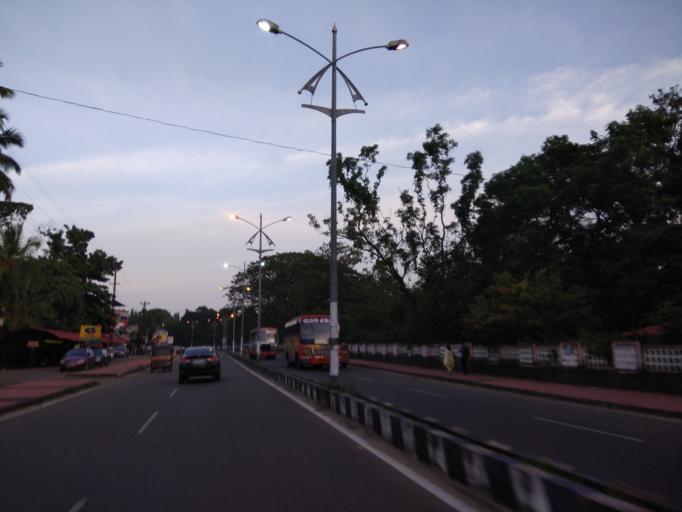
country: IN
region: Kerala
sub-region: Thrissur District
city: Trichur
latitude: 10.5230
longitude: 76.1902
